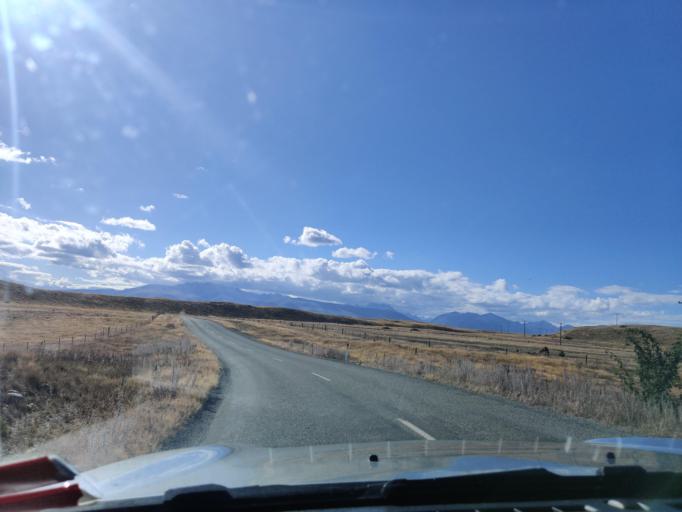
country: NZ
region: Canterbury
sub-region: Timaru District
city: Pleasant Point
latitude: -43.9944
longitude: 170.4514
